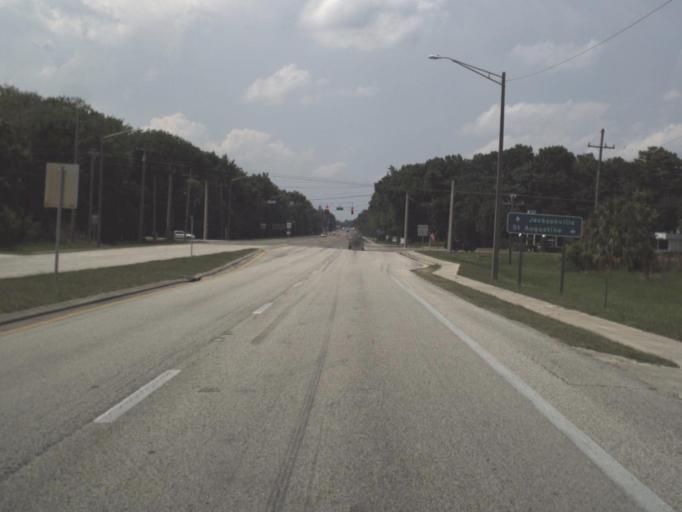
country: US
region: Florida
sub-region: Clay County
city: Green Cove Springs
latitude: 29.9818
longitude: -81.6754
